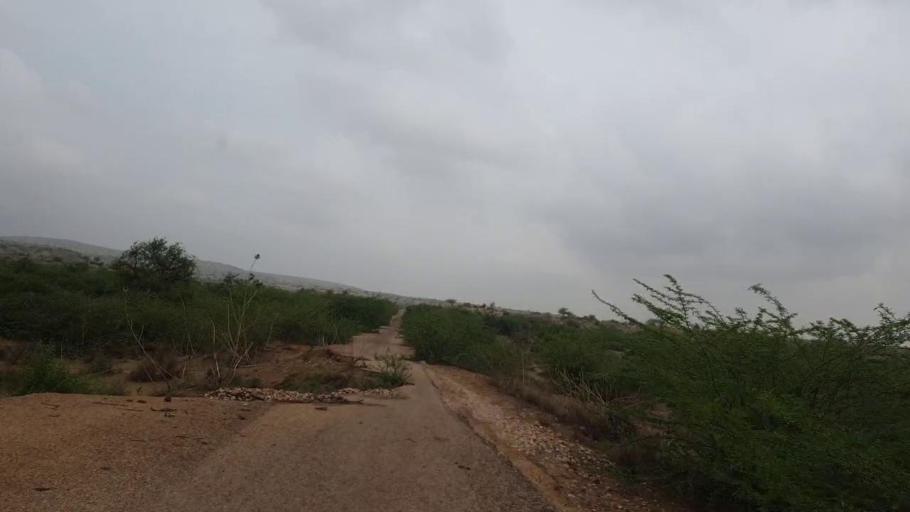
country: PK
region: Sindh
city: Diplo
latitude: 24.5159
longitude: 69.4727
